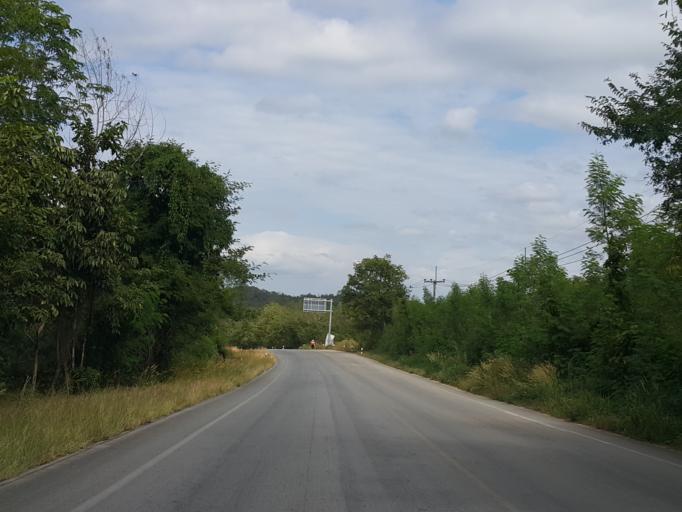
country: TH
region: Lampang
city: Lampang
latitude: 18.4044
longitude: 99.4532
